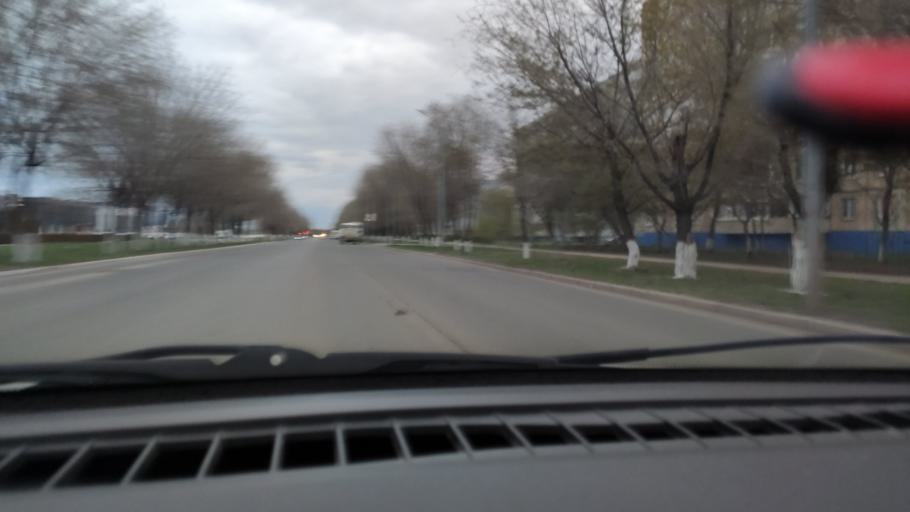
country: RU
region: Orenburg
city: Orenburg
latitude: 51.8455
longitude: 55.1337
